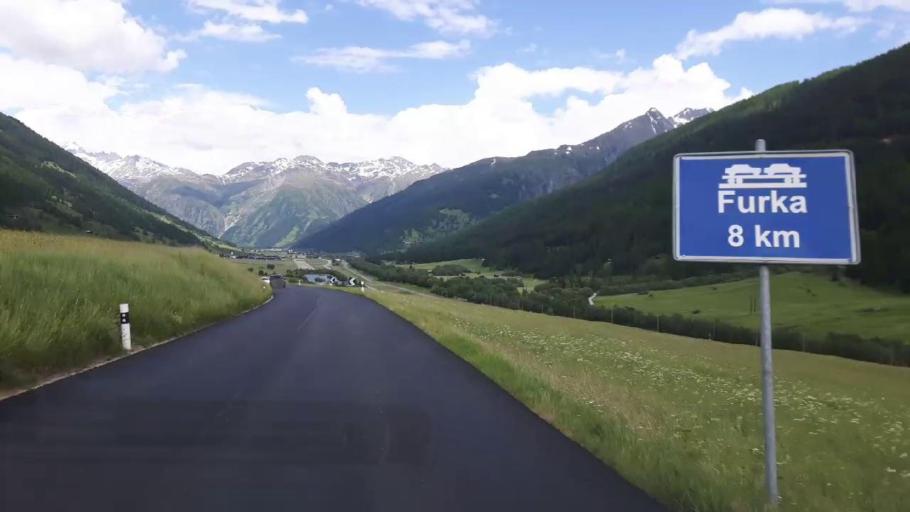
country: CH
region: Valais
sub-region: Goms District
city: Fiesch
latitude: 46.4895
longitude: 8.2741
